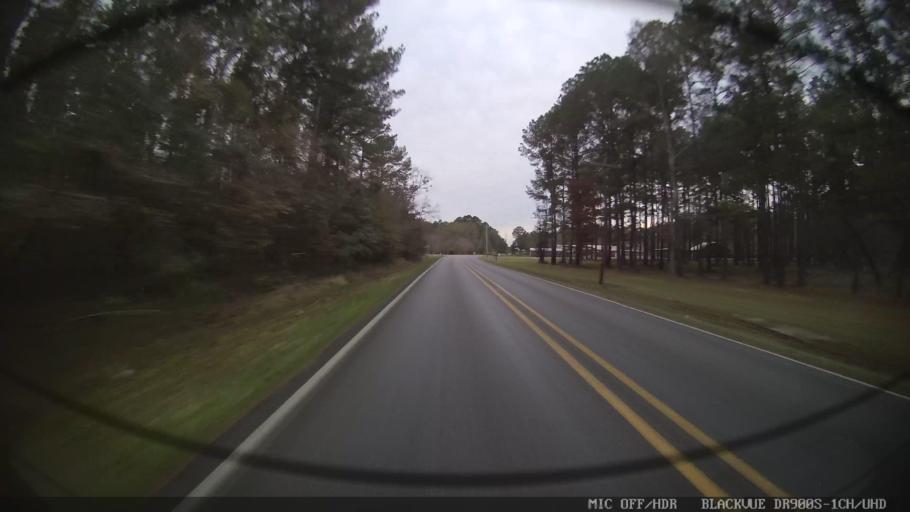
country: US
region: Mississippi
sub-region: Clarke County
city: Quitman
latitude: 32.0293
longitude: -88.7961
